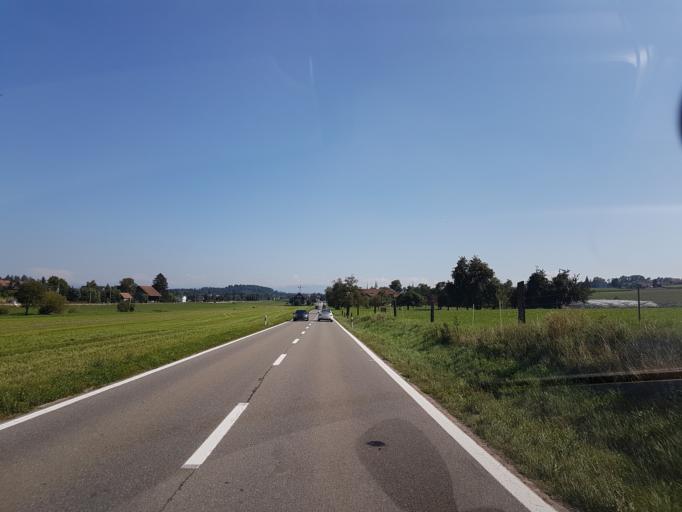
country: CH
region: Aargau
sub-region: Bezirk Muri
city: Muri
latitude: 47.2869
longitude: 8.3265
